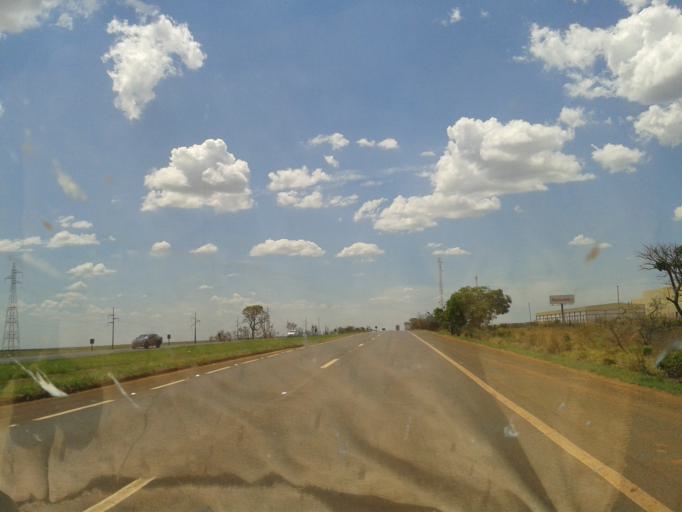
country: BR
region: Minas Gerais
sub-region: Uberlandia
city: Uberlandia
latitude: -19.0759
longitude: -48.1886
